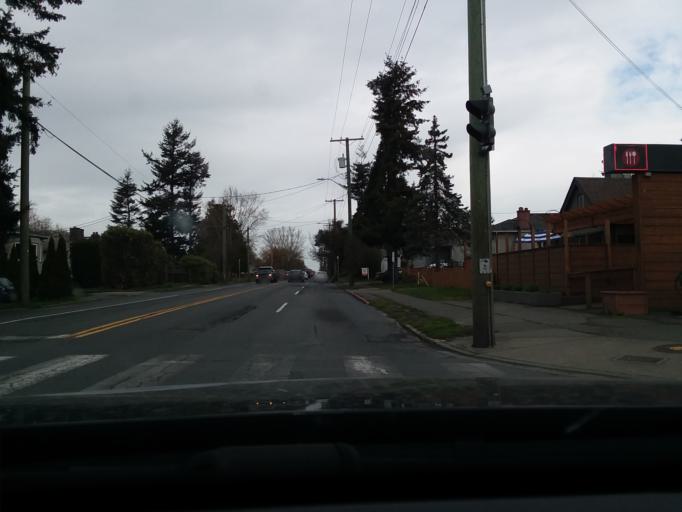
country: CA
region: British Columbia
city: Oak Bay
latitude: 48.4506
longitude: -123.3331
